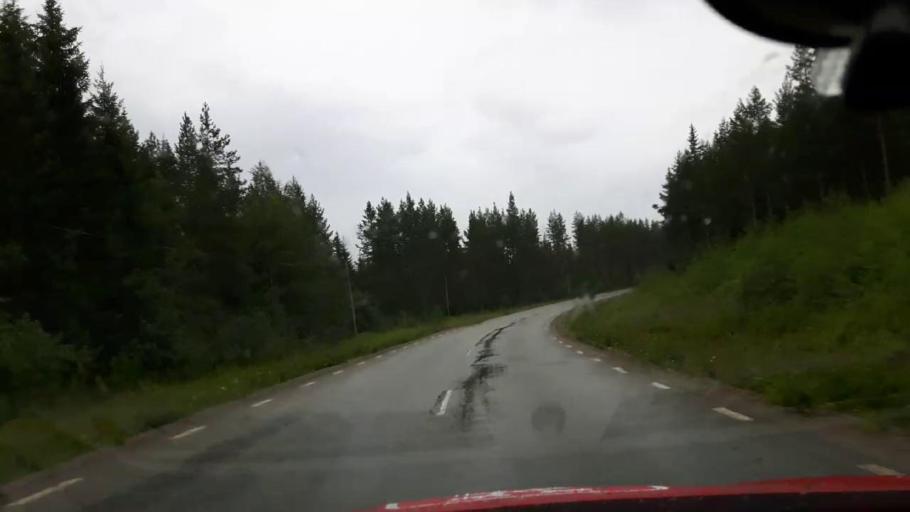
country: SE
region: Jaemtland
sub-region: OEstersunds Kommun
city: Brunflo
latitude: 62.8317
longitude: 15.0080
